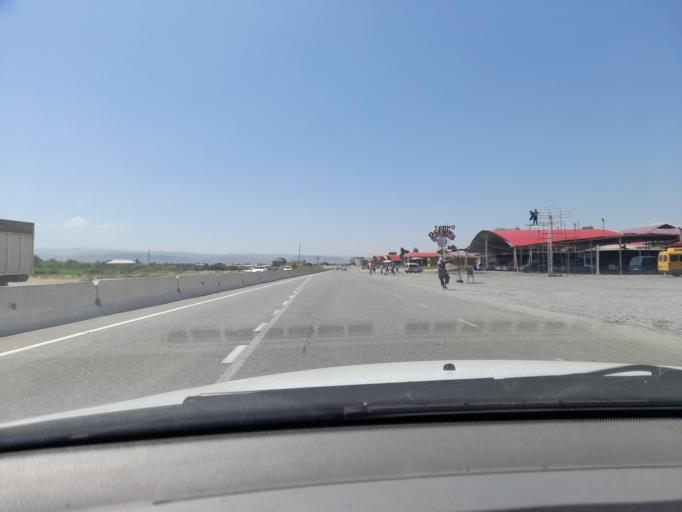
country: UZ
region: Jizzax
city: Jizzax
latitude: 40.0822
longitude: 67.9284
